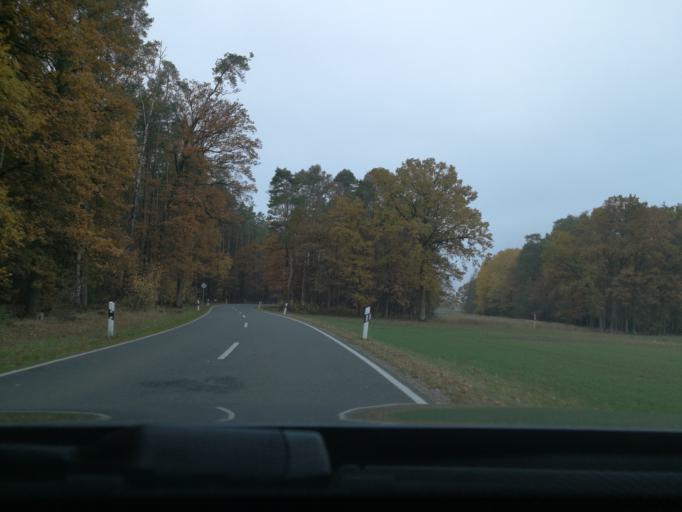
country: DE
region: Bavaria
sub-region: Regierungsbezirk Mittelfranken
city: Puschendorf
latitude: 49.5619
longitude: 10.8405
